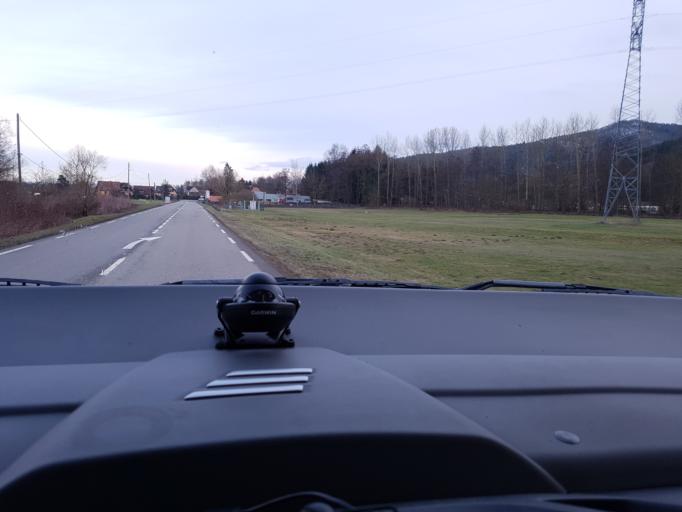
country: FR
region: Alsace
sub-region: Departement du Bas-Rhin
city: Chatenois
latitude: 48.2876
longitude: 7.3749
